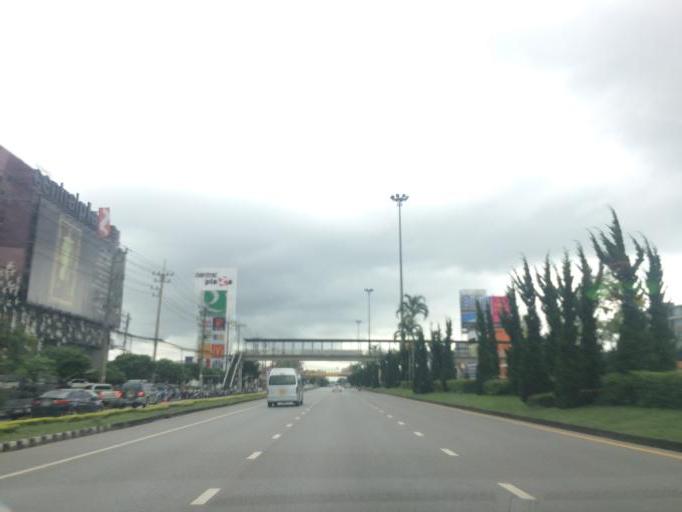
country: TH
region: Chiang Rai
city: Chiang Rai
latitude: 19.8857
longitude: 99.8352
